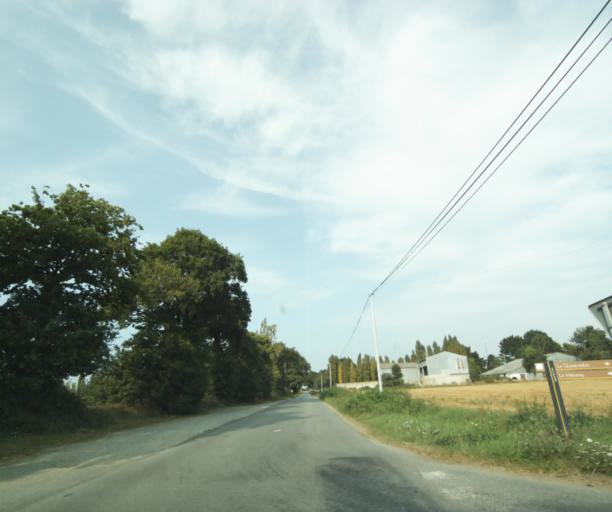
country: FR
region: Brittany
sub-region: Departement des Cotes-d'Armor
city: Jugon-les-Lacs
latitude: 48.4265
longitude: -2.3056
